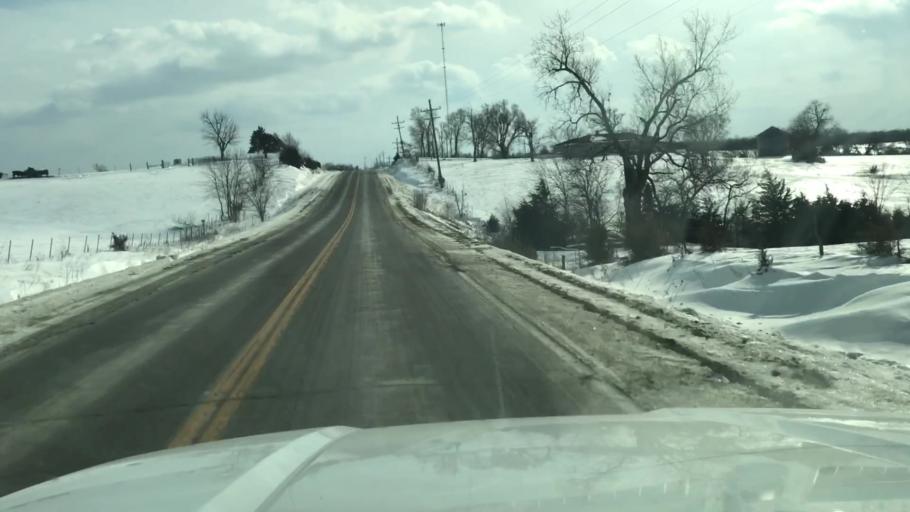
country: US
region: Missouri
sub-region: Gentry County
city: Stanberry
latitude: 40.3759
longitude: -94.6472
